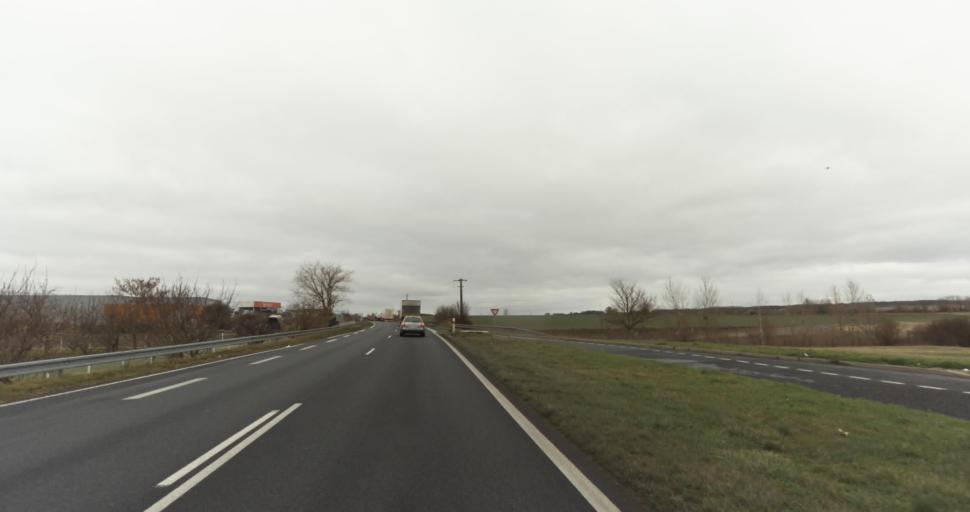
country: FR
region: Pays de la Loire
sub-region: Departement de Maine-et-Loire
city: Doue-la-Fontaine
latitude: 47.1891
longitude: -0.2432
